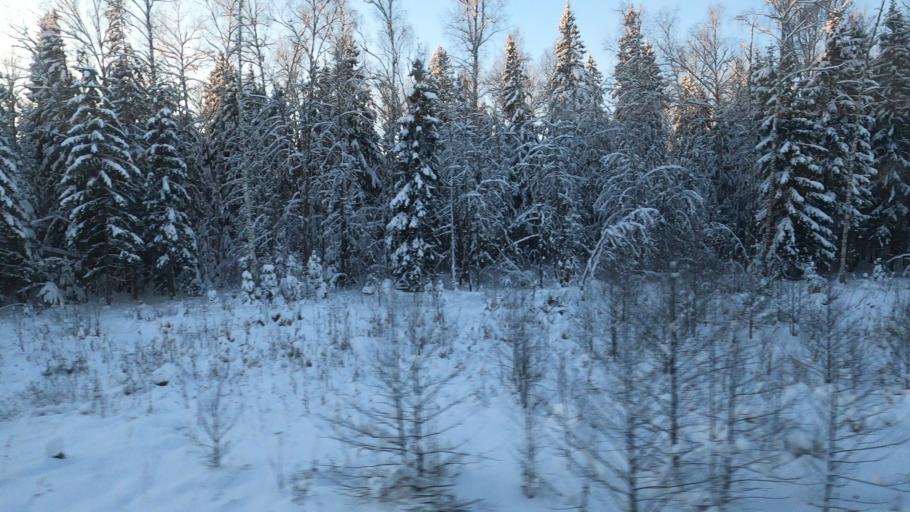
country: RU
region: Moskovskaya
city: Zhukovka
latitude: 56.4976
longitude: 37.5522
